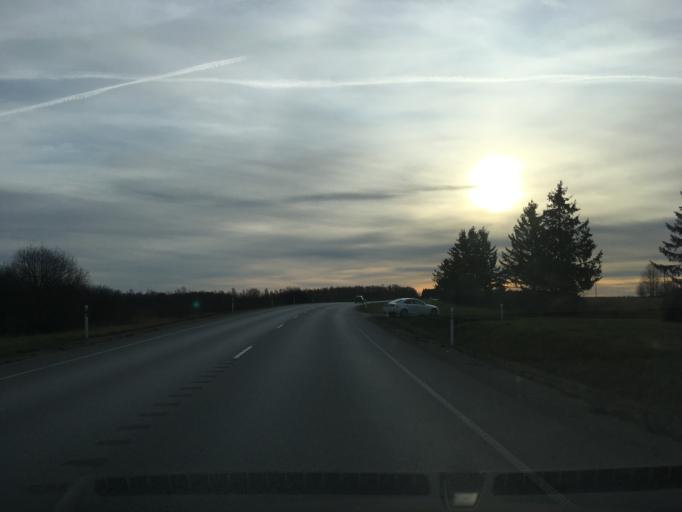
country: EE
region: Ida-Virumaa
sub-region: Kivioli linn
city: Kivioli
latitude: 59.4223
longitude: 26.9676
